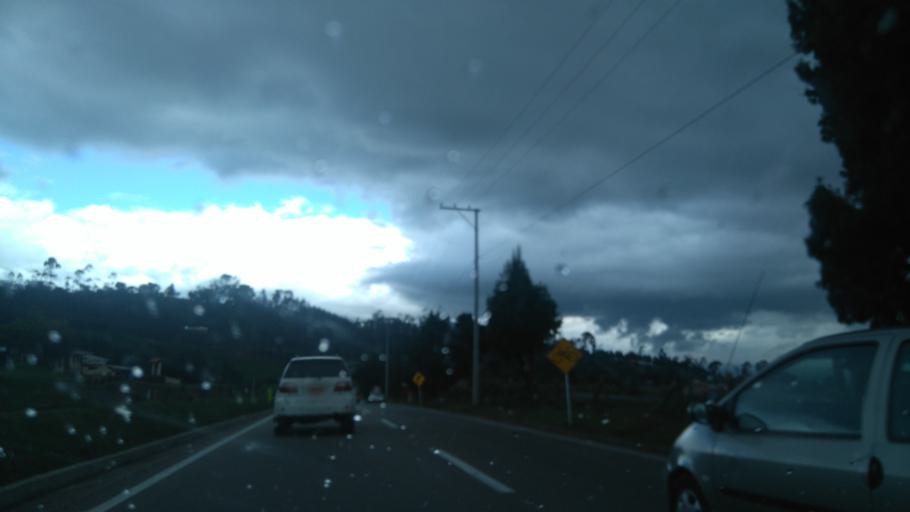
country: CO
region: Cundinamarca
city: El Rosal
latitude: 4.8722
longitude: -74.2915
